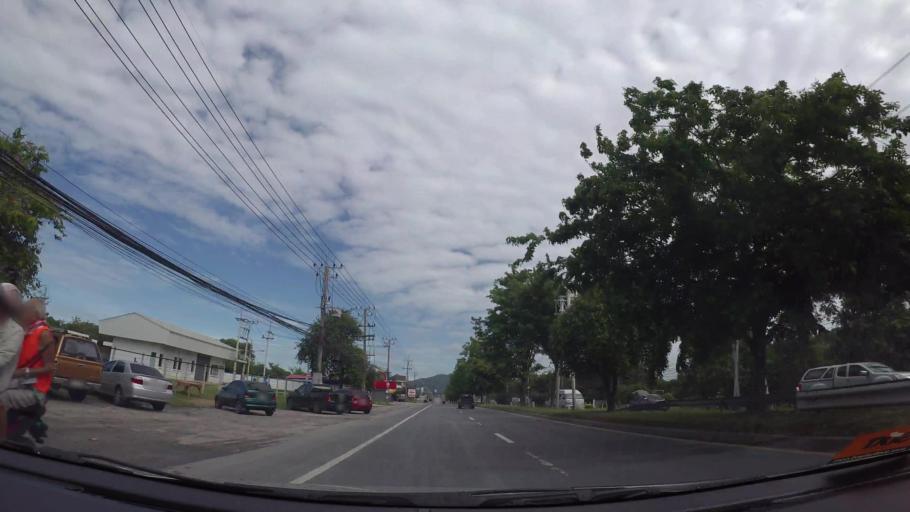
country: TH
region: Rayong
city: Ban Chang
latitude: 12.7319
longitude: 101.1365
